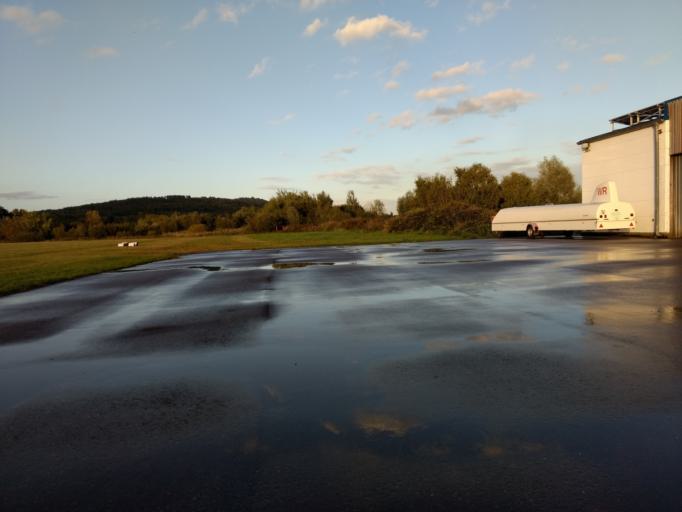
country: DE
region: Saarland
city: Nalbach
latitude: 49.3871
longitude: 6.7520
